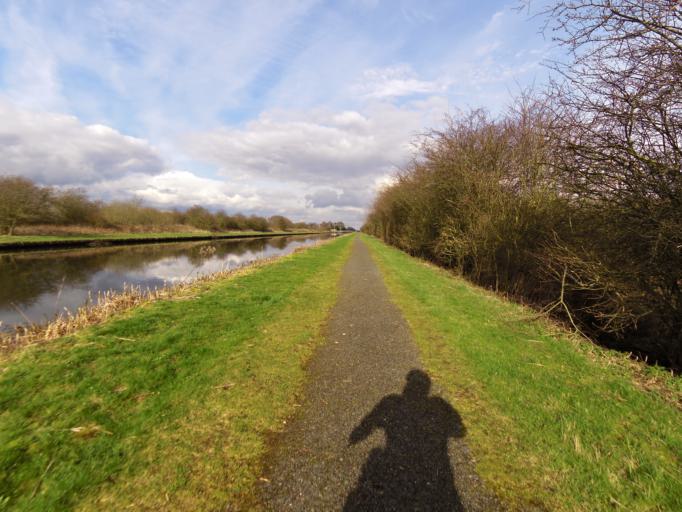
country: GB
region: England
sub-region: Doncaster
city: Stainforth
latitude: 53.6448
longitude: -1.0295
